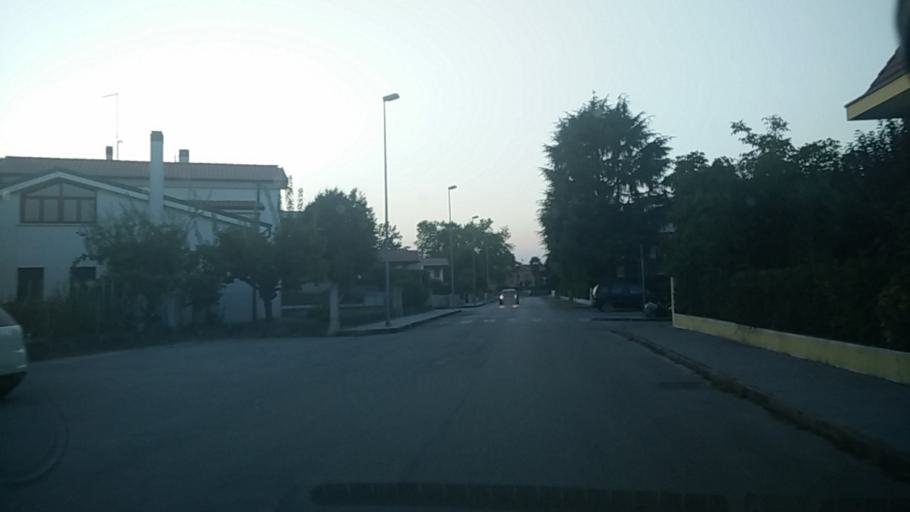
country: IT
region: Veneto
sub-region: Provincia di Venezia
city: San Dona di Piave
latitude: 45.6421
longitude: 12.5580
